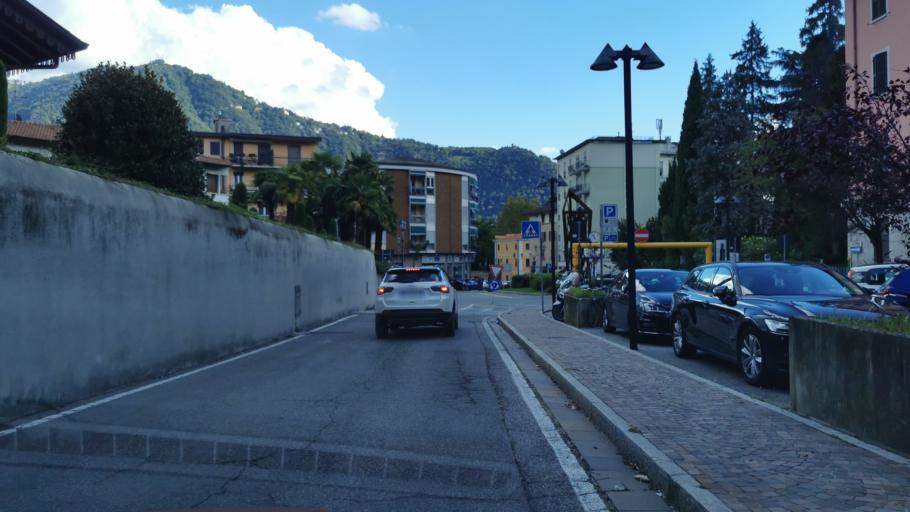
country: IT
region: Lombardy
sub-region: Provincia di Como
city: Cernobbio
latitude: 45.8419
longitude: 9.0741
